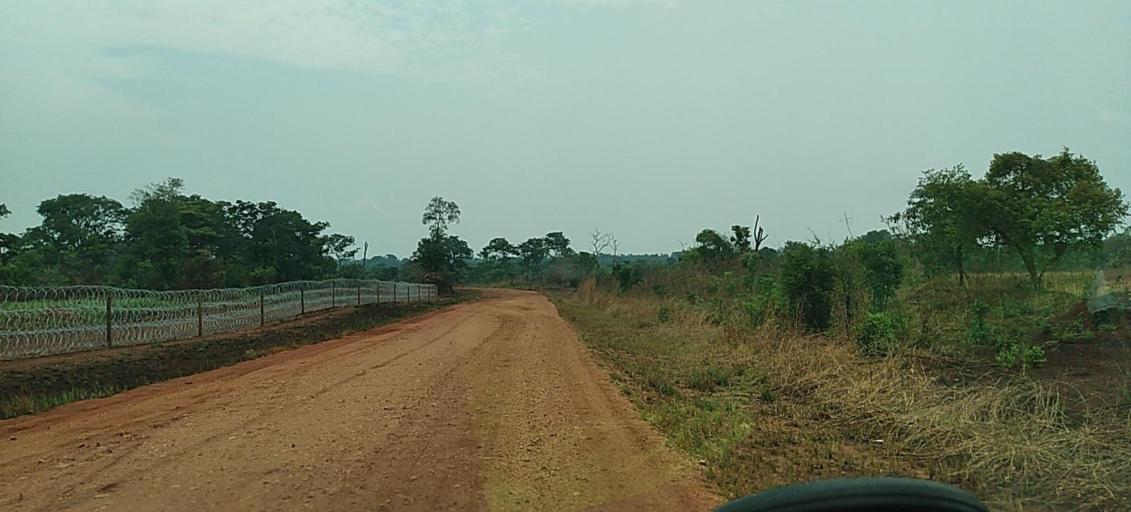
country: ZM
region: North-Western
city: Kansanshi
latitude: -12.1112
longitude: 26.4876
